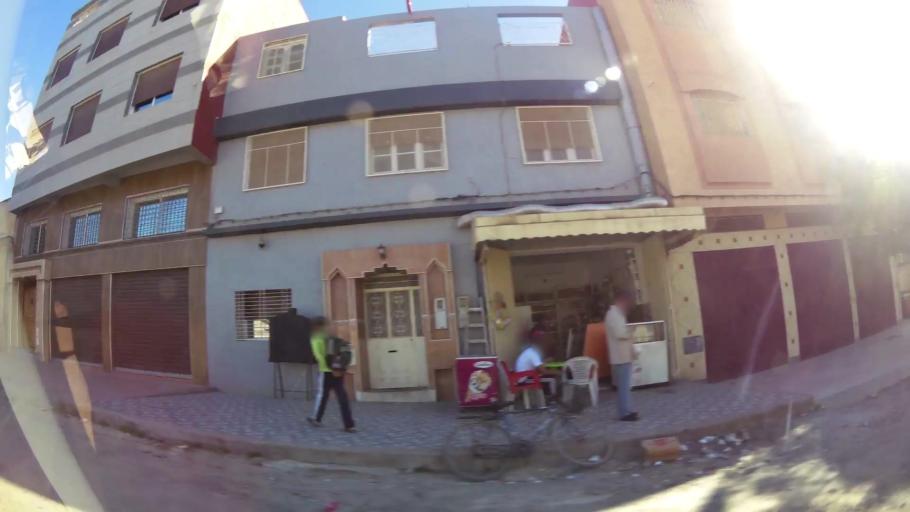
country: MA
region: Oriental
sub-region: Berkane-Taourirt
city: Ahfir
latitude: 34.9546
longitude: -2.1004
